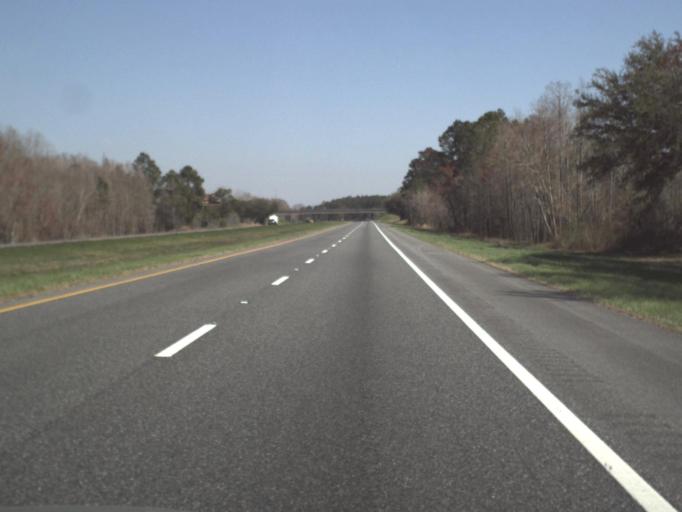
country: US
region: Florida
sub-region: Washington County
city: Chipley
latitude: 30.7470
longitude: -85.4223
